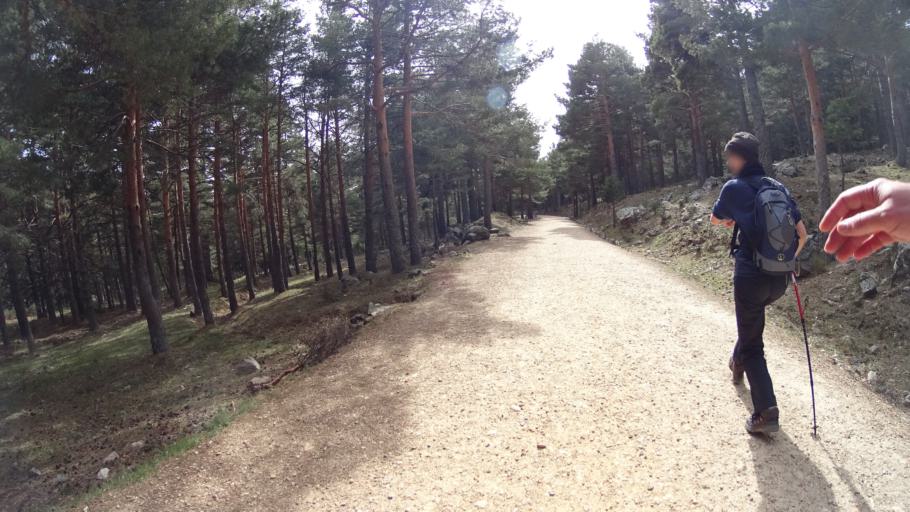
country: ES
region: Madrid
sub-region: Provincia de Madrid
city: Navacerrada
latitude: 40.7652
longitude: -3.9958
